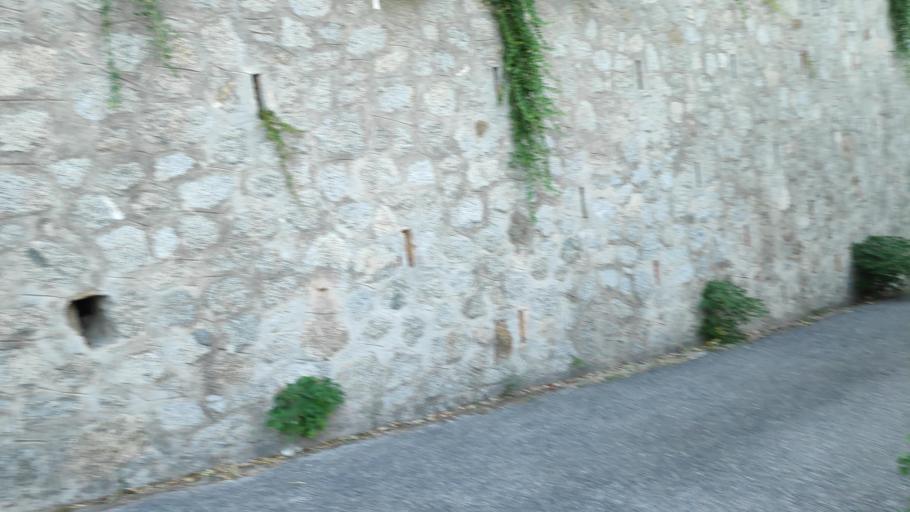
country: IT
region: Calabria
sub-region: Provincia di Catanzaro
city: Soverato Marina
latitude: 38.6899
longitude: 16.5455
